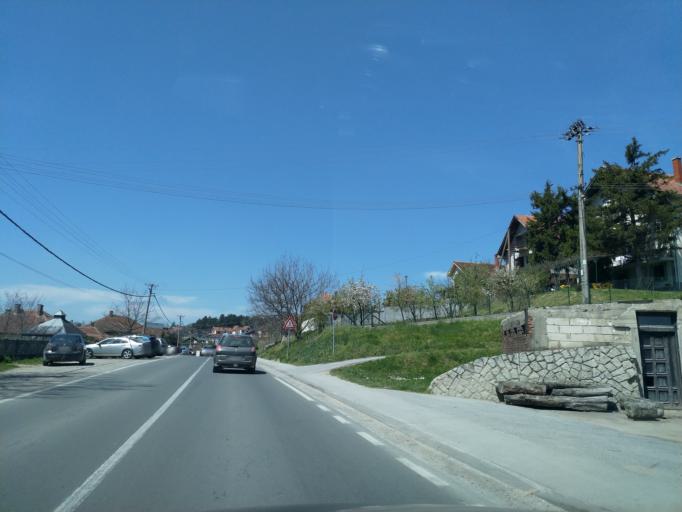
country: RS
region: Central Serbia
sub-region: Sumadijski Okrug
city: Arangelovac
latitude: 44.3274
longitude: 20.5226
